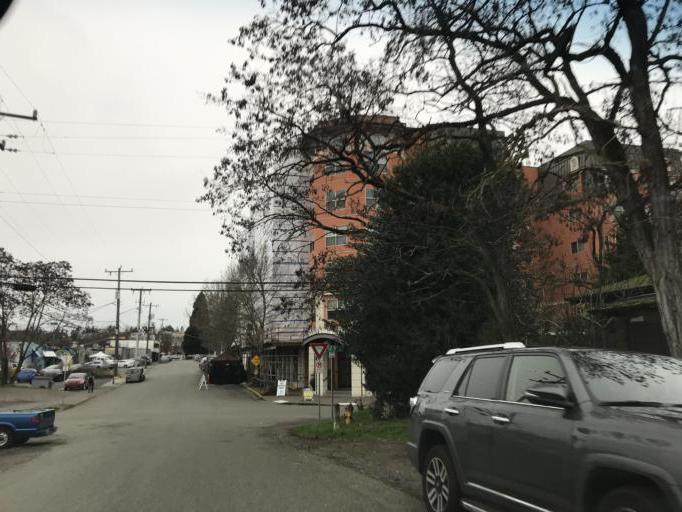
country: US
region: Washington
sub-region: King County
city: Lake Forest Park
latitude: 47.7171
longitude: -122.2952
